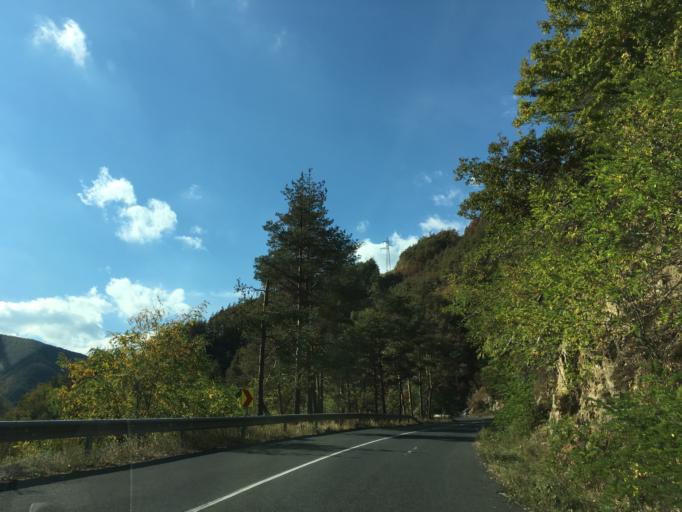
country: BG
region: Smolyan
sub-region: Obshtina Nedelino
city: Nedelino
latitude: 41.4386
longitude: 25.0189
